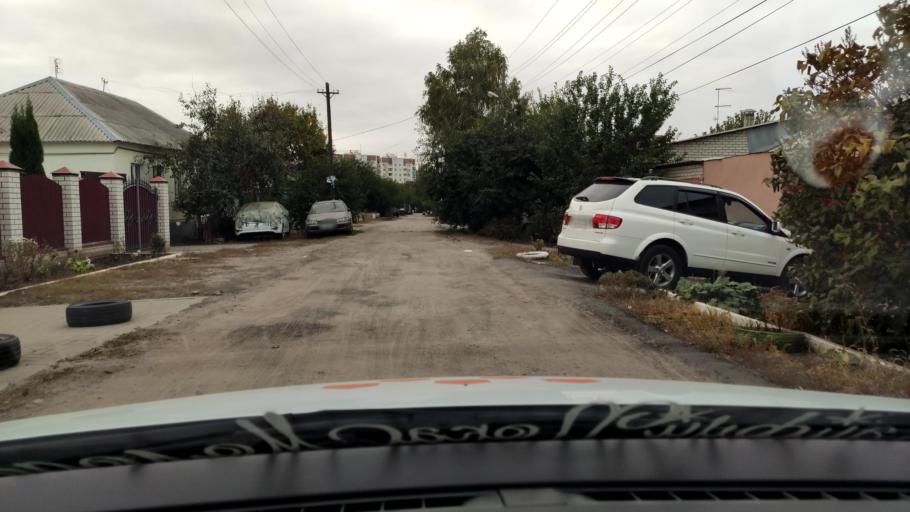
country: RU
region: Voronezj
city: Voronezh
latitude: 51.6756
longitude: 39.1649
